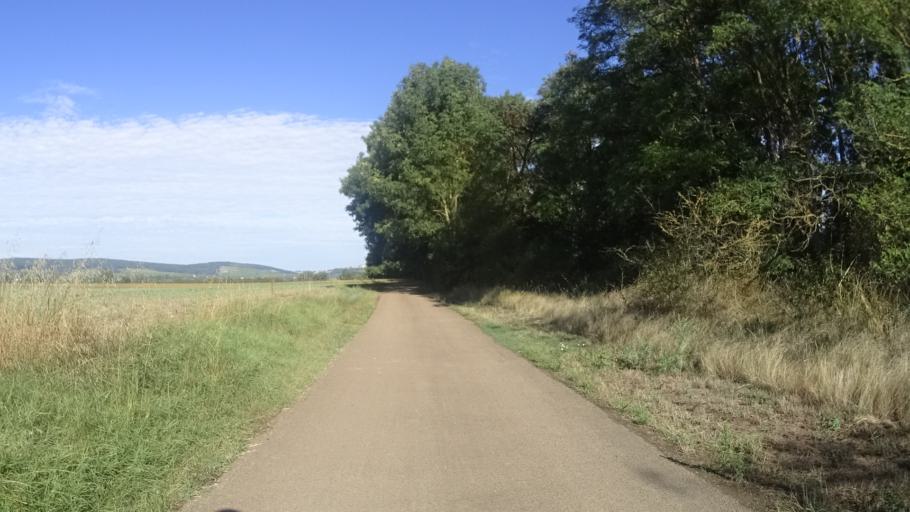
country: FR
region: Bourgogne
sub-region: Departement de la Nievre
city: Pouilly-sur-Loire
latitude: 47.3061
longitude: 2.8994
